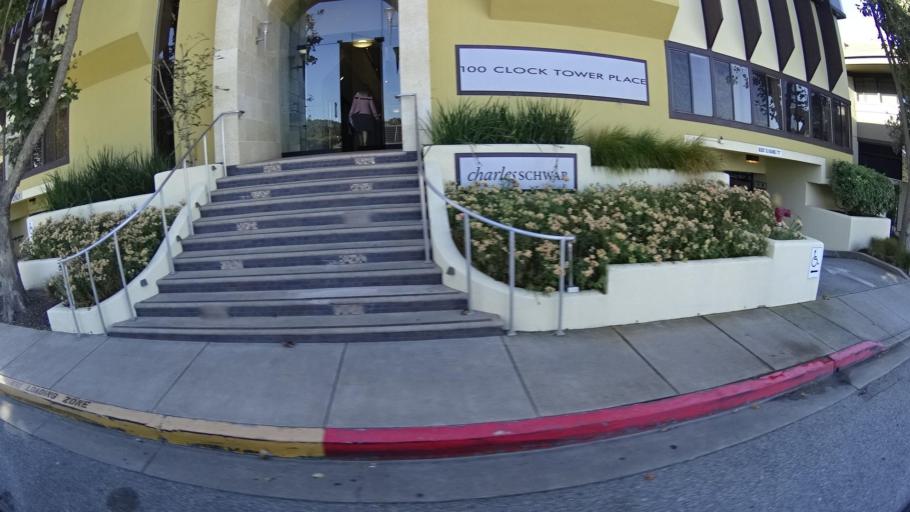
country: US
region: California
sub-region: Monterey County
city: Carmel-by-the-Sea
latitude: 36.5398
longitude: -121.9054
